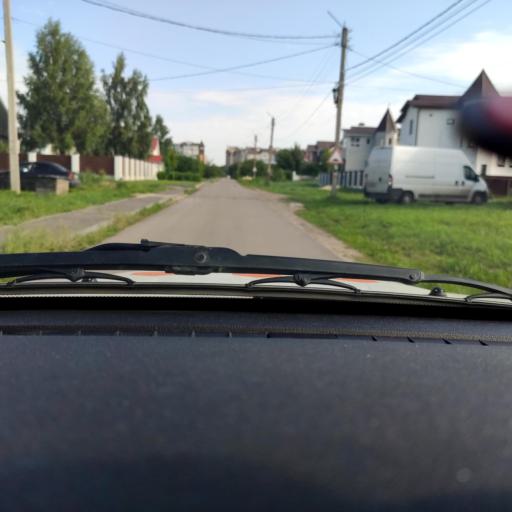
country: RU
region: Voronezj
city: Novaya Usman'
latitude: 51.6466
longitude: 39.3330
